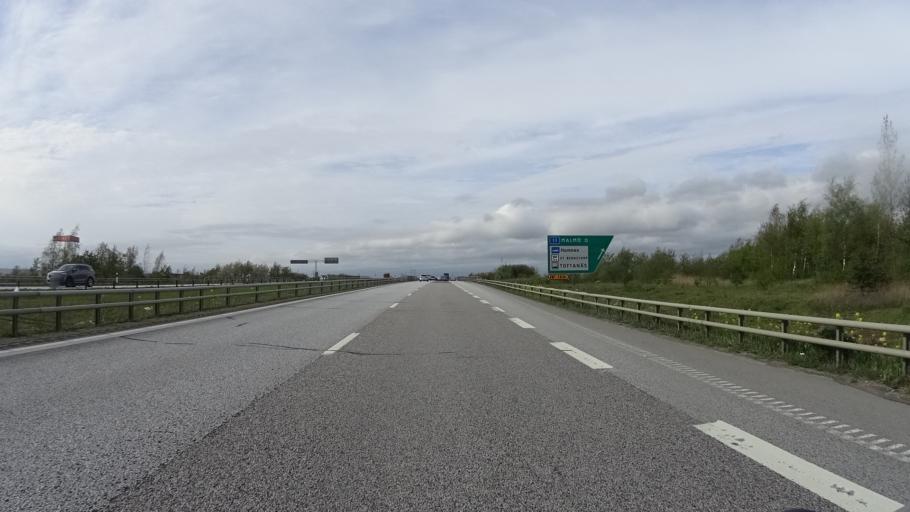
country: SE
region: Skane
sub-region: Burlovs Kommun
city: Arloev
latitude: 55.6110
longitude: 13.1150
